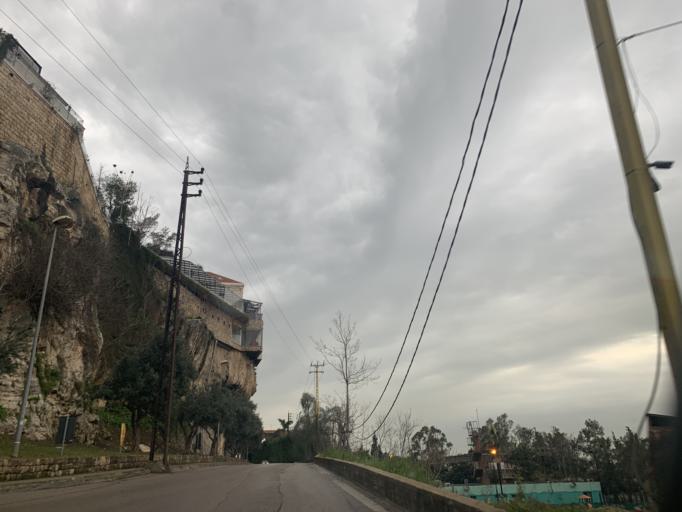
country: LB
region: Mont-Liban
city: Djounie
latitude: 33.9824
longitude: 35.6258
